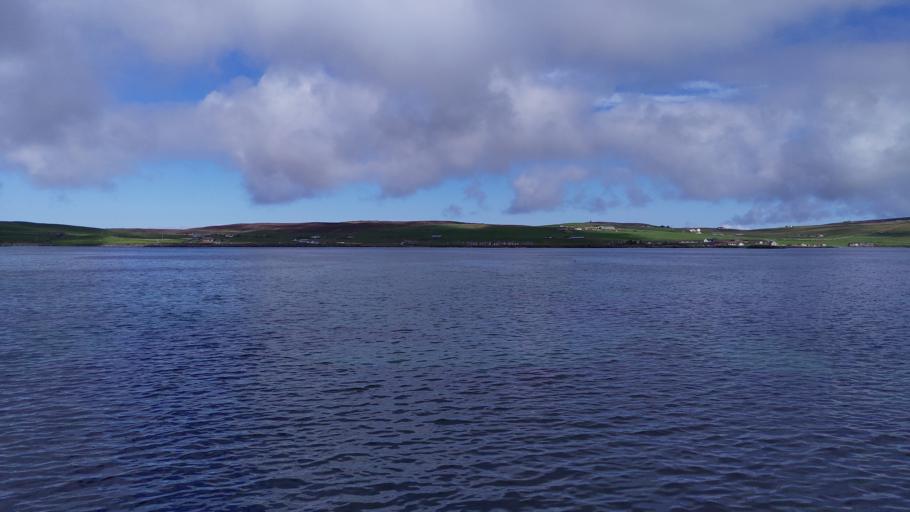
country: GB
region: Scotland
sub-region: Shetland Islands
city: Shetland
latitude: 60.1524
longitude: -1.1368
